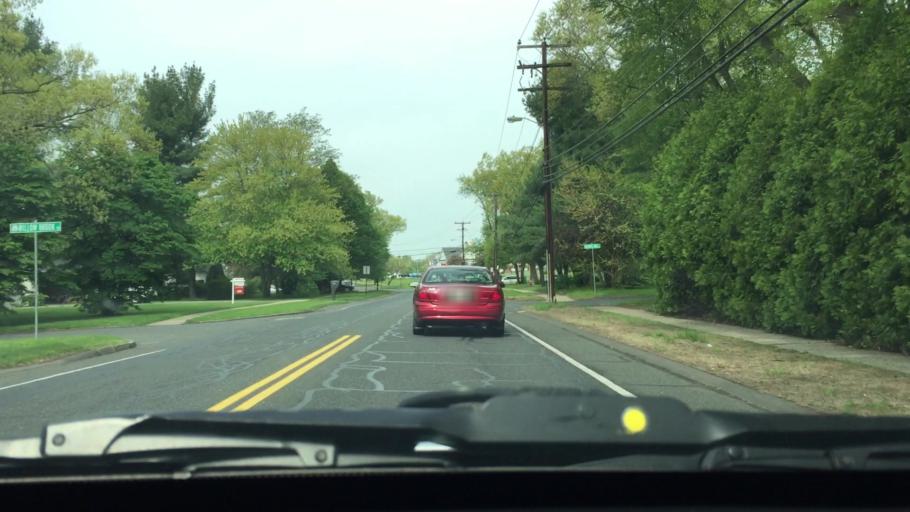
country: US
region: Massachusetts
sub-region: Hampden County
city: Longmeadow
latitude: 42.0565
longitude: -72.5484
